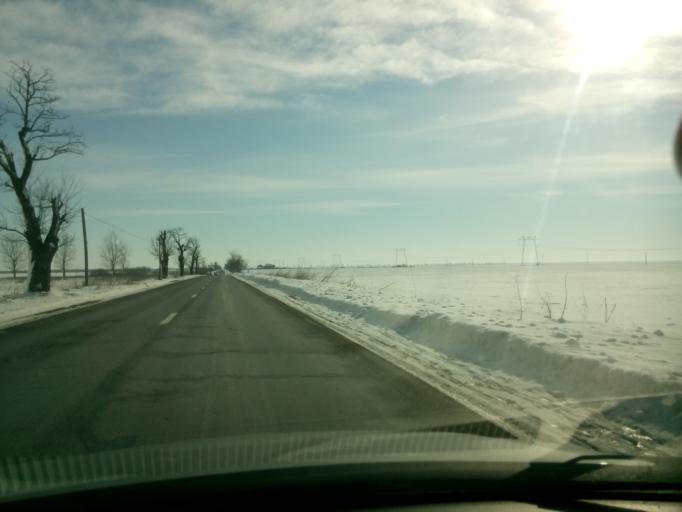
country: RO
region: Calarasi
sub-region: Comuna Frumusani
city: Frumusani
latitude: 44.2696
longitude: 26.3458
